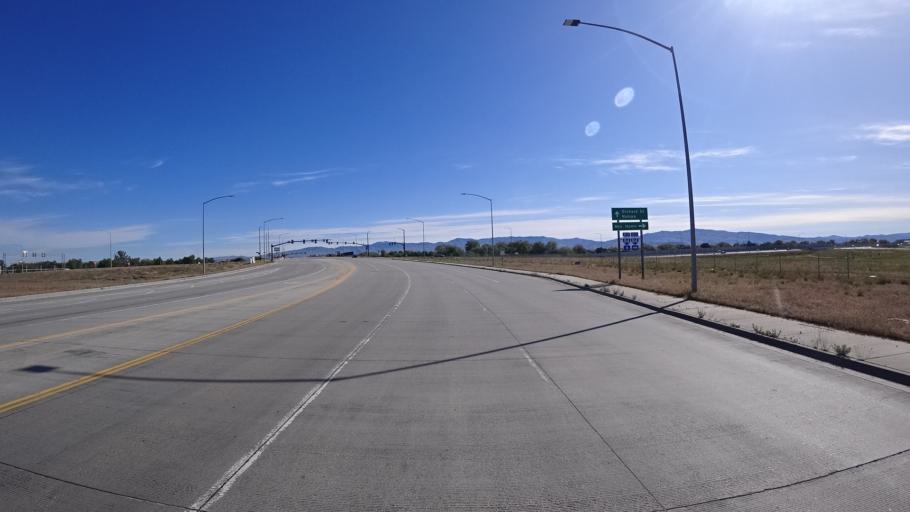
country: US
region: Idaho
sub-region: Ada County
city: Garden City
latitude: 43.5734
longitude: -116.2452
